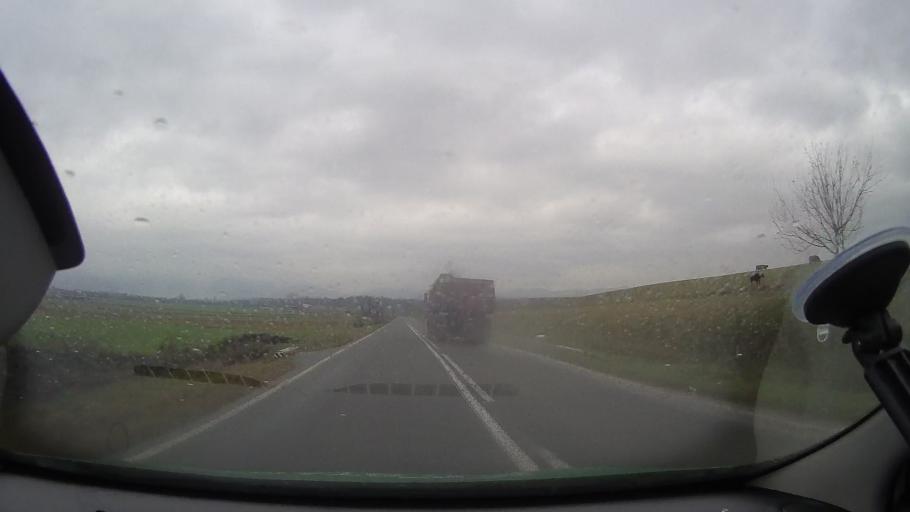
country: RO
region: Arad
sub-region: Comuna Dieci
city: Dieci
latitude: 46.2789
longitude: 22.2890
